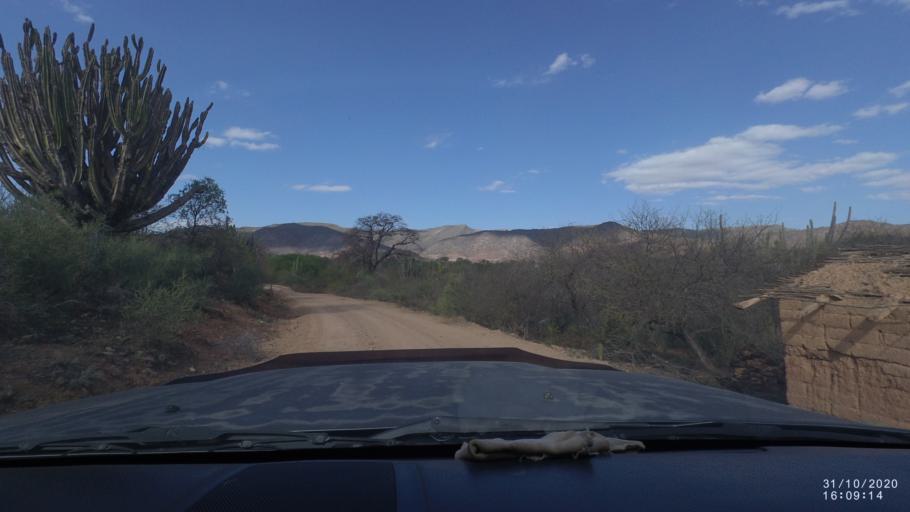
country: BO
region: Chuquisaca
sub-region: Provincia Zudanez
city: Mojocoya
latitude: -18.3870
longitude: -64.6377
